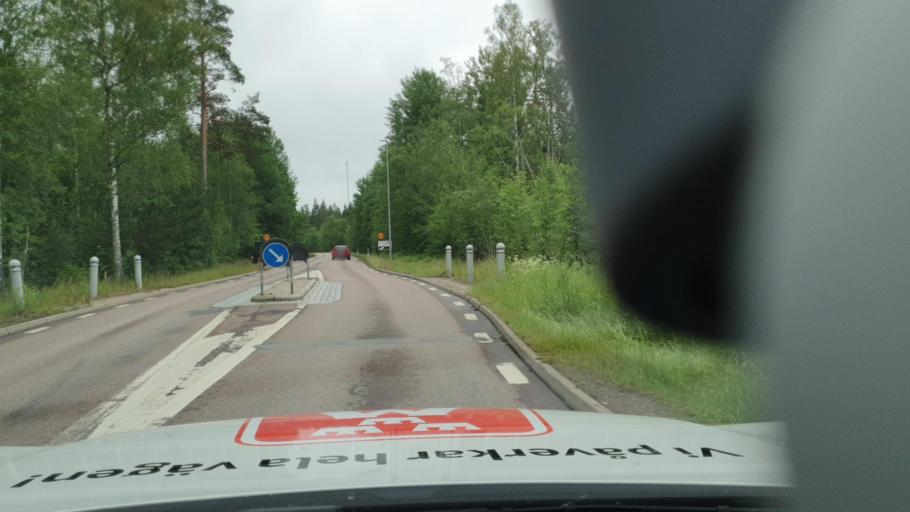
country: SE
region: Vaermland
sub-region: Kristinehamns Kommun
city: Bjorneborg
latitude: 59.2397
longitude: 14.2552
